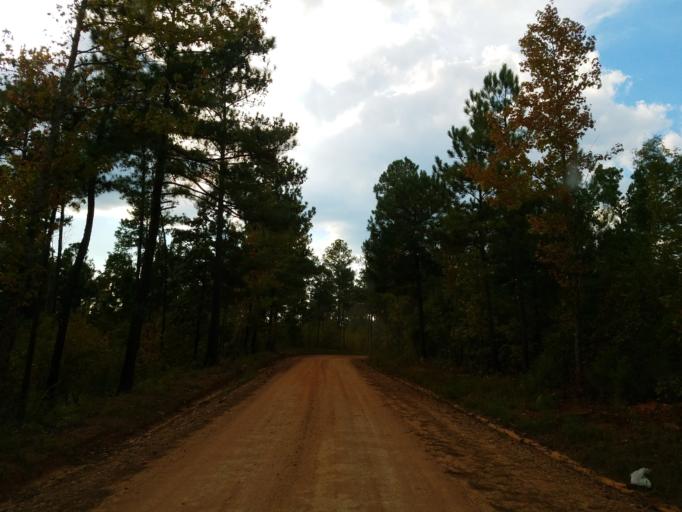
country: US
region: Georgia
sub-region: Monroe County
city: Forsyth
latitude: 33.1149
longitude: -84.0199
